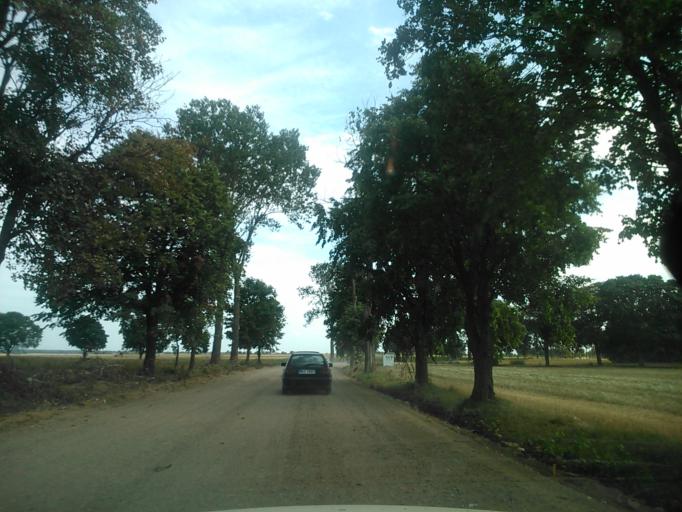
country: PL
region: Warmian-Masurian Voivodeship
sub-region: Powiat dzialdowski
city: Ilowo -Osada
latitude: 53.1948
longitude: 20.2679
